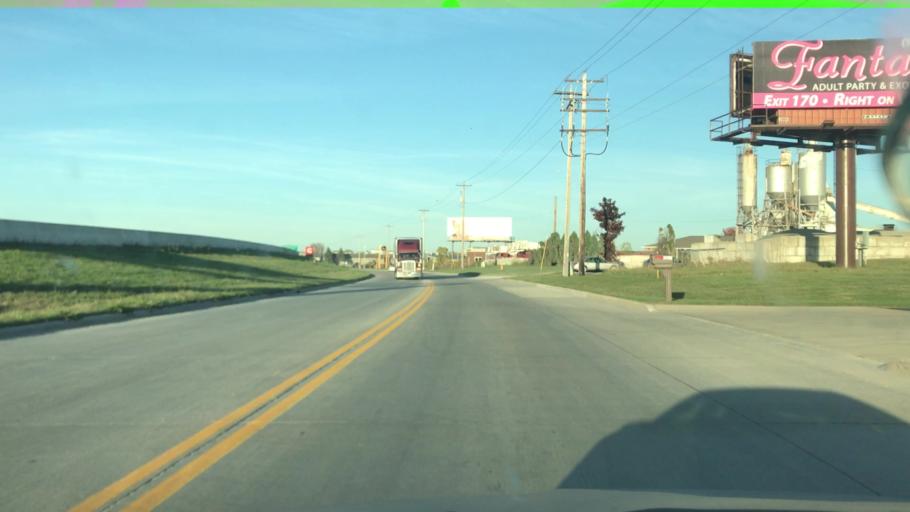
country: US
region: Wisconsin
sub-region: Brown County
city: De Pere
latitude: 44.4370
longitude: -88.1011
